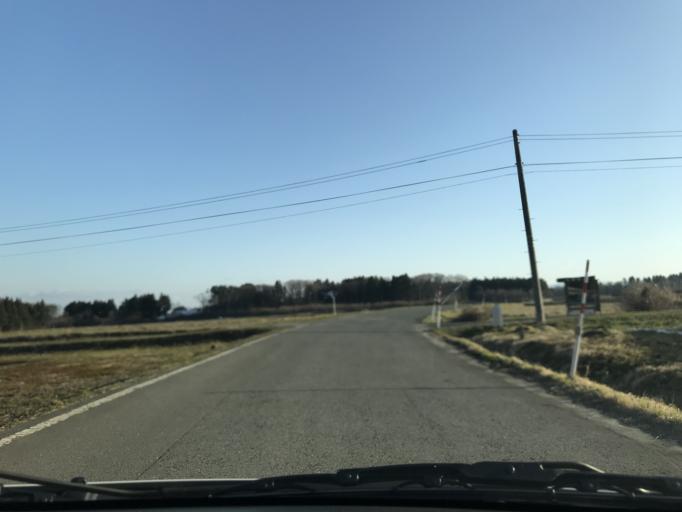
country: JP
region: Iwate
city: Kitakami
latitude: 39.2311
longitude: 141.0448
